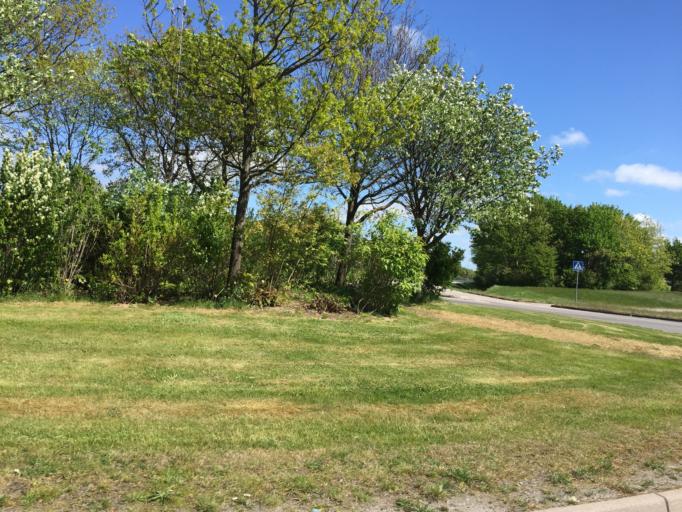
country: SE
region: Halland
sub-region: Varbergs Kommun
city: Varberg
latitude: 57.1112
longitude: 12.2920
